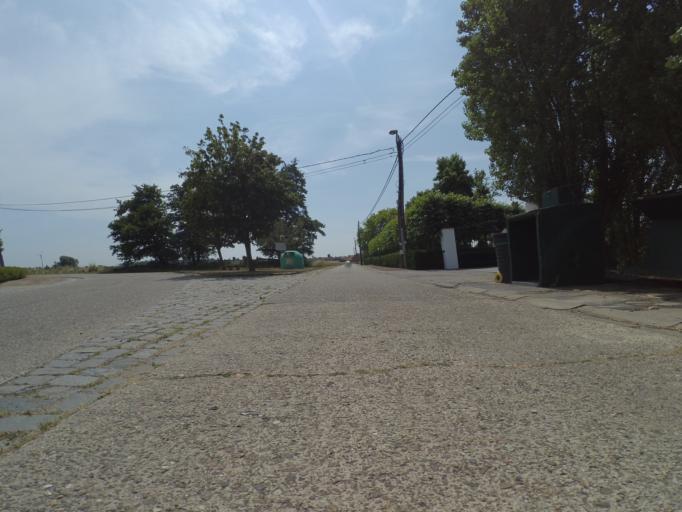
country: BE
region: Flanders
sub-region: Provincie Antwerpen
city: Brecht
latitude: 51.3879
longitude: 4.6334
